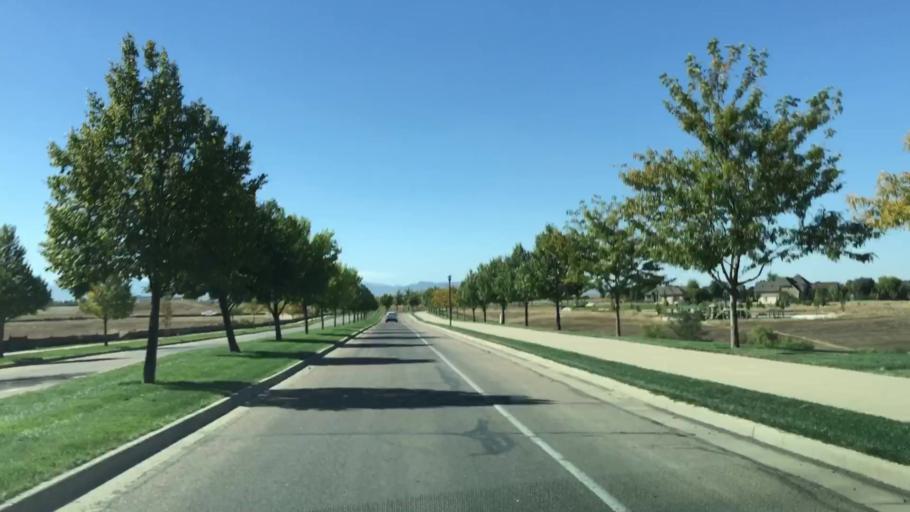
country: US
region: Colorado
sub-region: Weld County
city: Windsor
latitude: 40.4431
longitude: -104.9705
